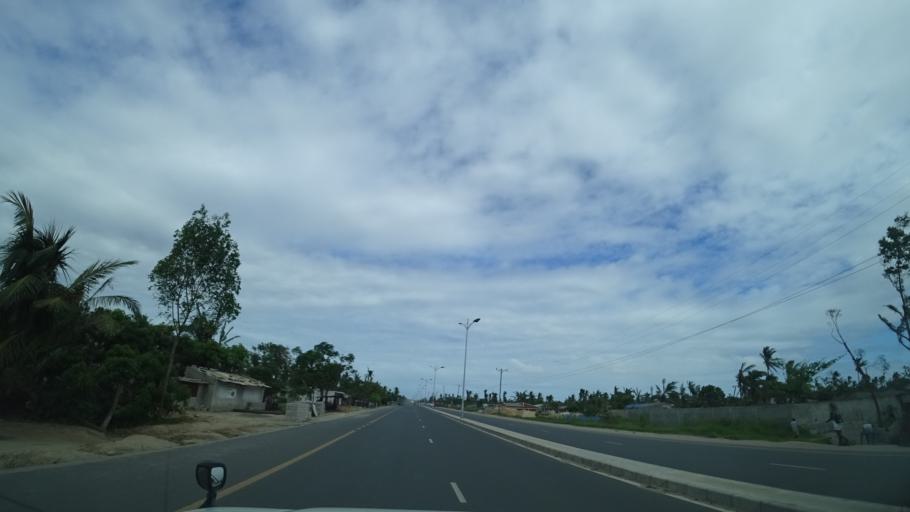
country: MZ
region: Sofala
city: Beira
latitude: -19.7559
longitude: 34.8774
